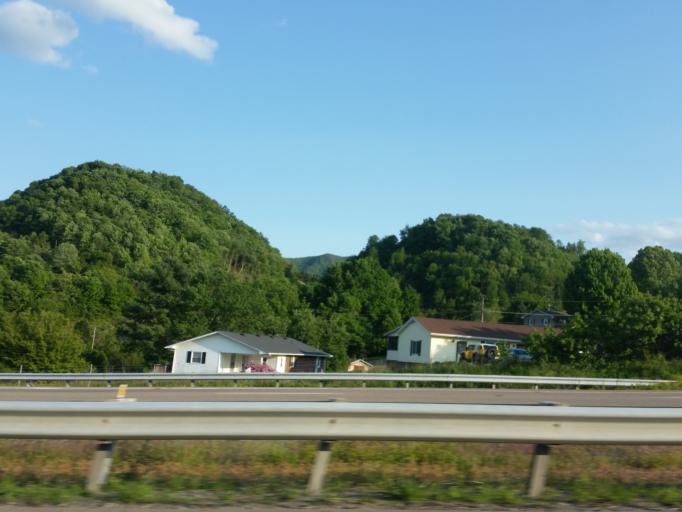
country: US
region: Virginia
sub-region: Russell County
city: Lebanon
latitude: 36.8980
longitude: -82.0635
